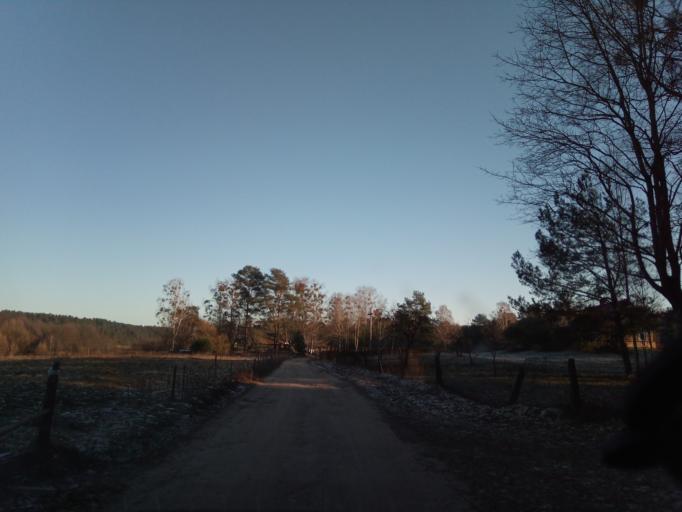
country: LT
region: Alytaus apskritis
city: Druskininkai
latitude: 53.9744
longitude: 23.9463
